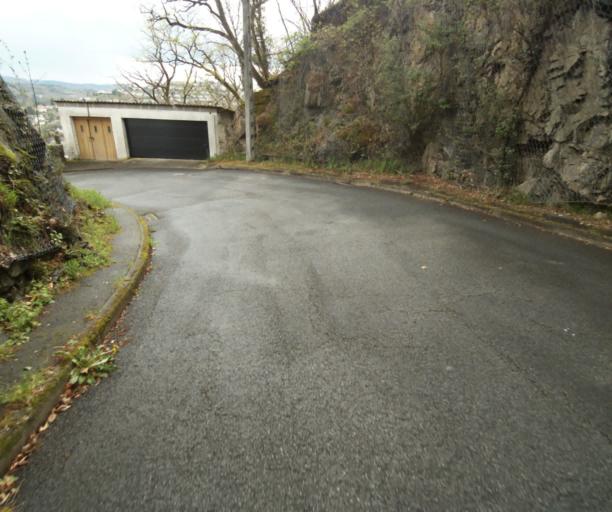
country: FR
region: Limousin
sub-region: Departement de la Correze
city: Tulle
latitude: 45.2636
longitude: 1.7570
